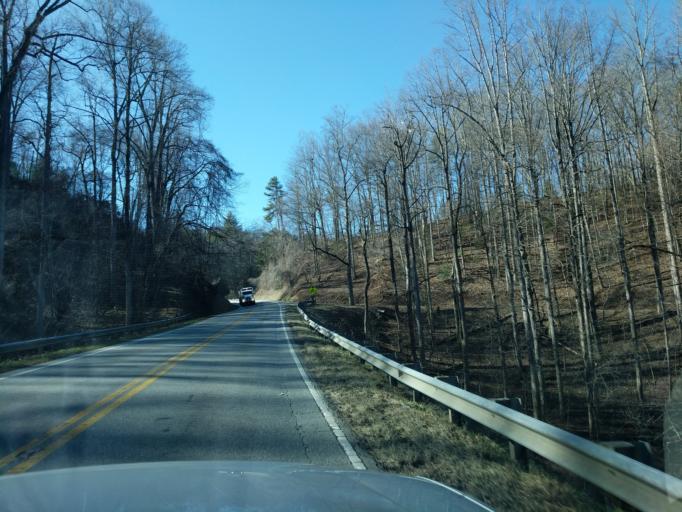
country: US
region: North Carolina
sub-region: Swain County
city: Bryson City
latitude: 35.3370
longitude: -83.5709
